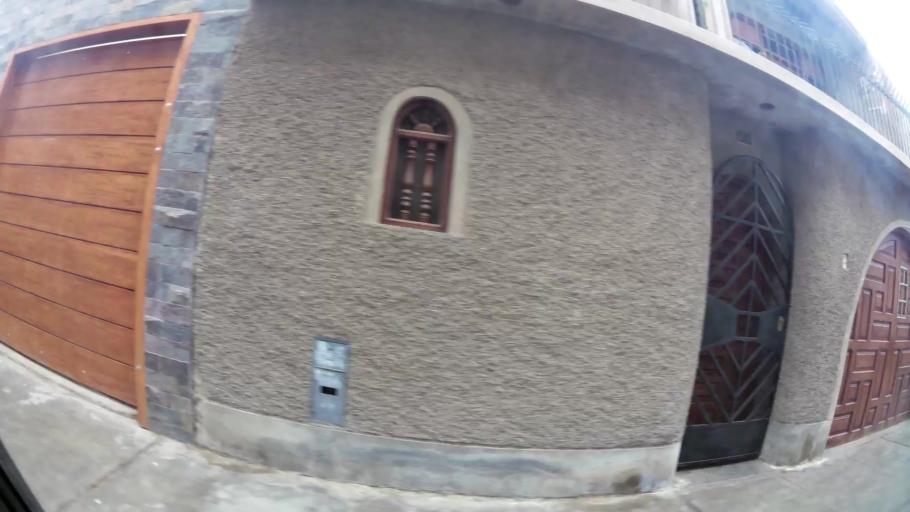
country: PE
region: La Libertad
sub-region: Provincia de Trujillo
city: Trujillo
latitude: -8.1230
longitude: -79.0301
